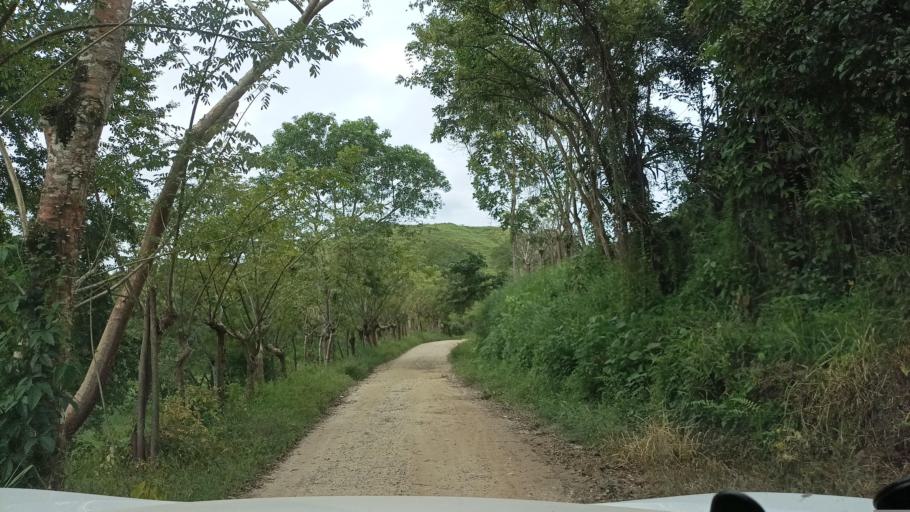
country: MX
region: Veracruz
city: Hidalgotitlan
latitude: 17.5918
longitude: -94.4217
